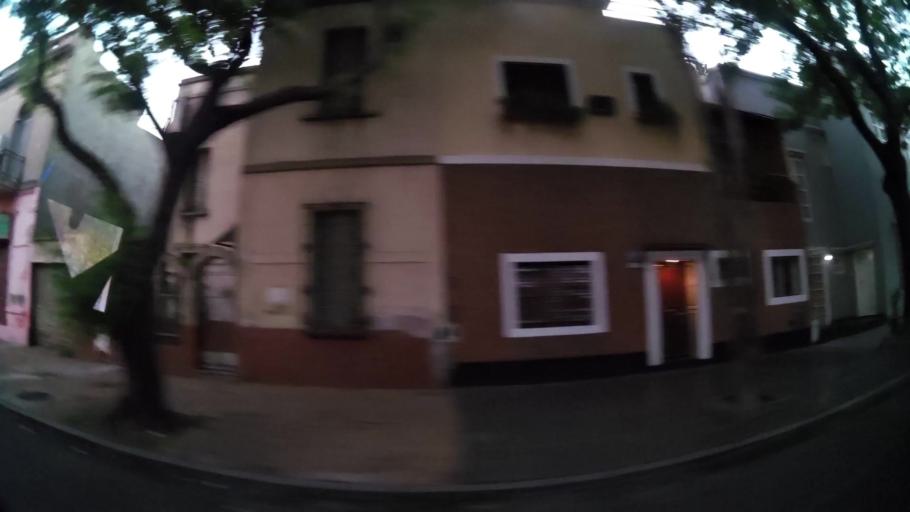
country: AR
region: Buenos Aires F.D.
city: Villa Santa Rita
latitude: -34.6346
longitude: -58.4376
